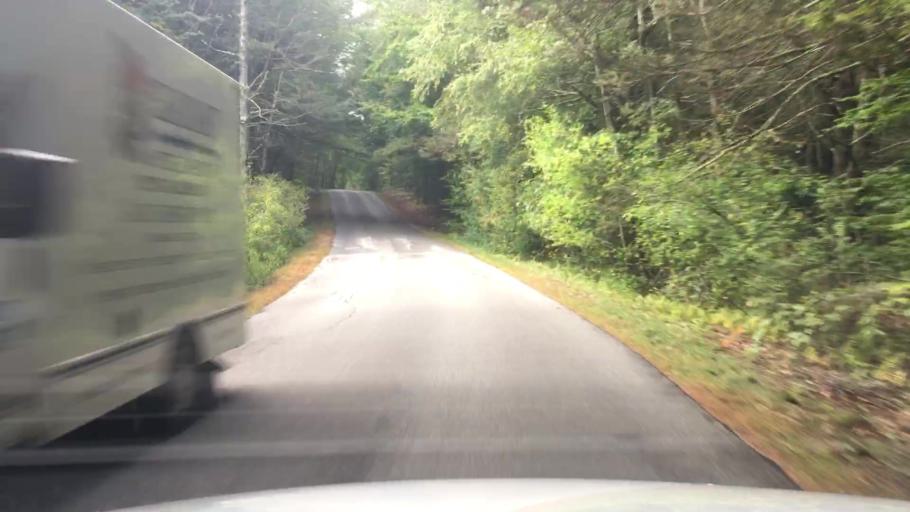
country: US
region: Maine
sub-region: York County
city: York Harbor
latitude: 43.1185
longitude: -70.6810
